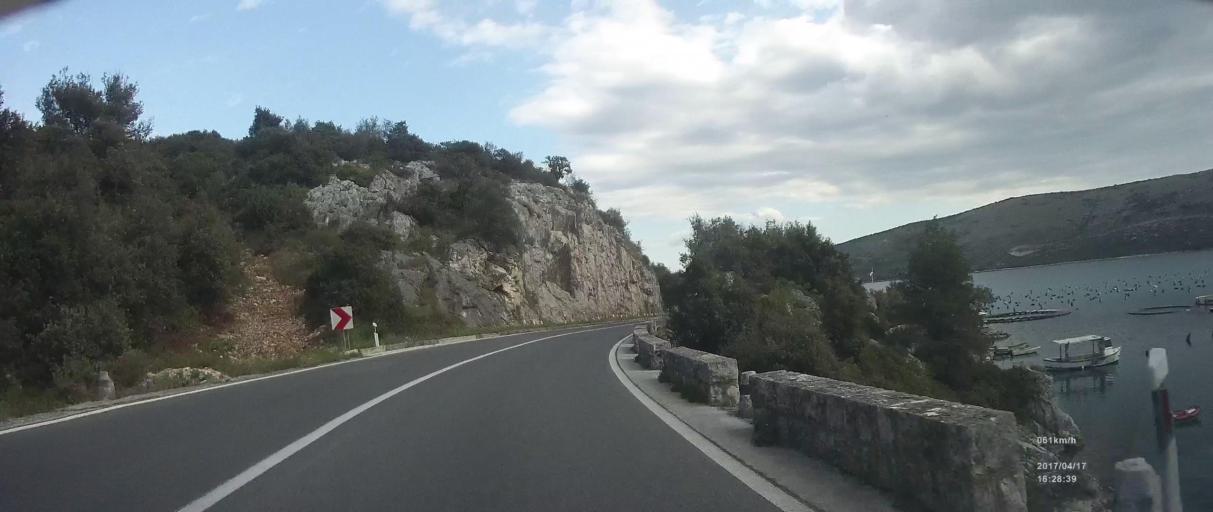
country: HR
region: Splitsko-Dalmatinska
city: Veliki Drvenik
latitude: 43.5159
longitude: 16.1567
